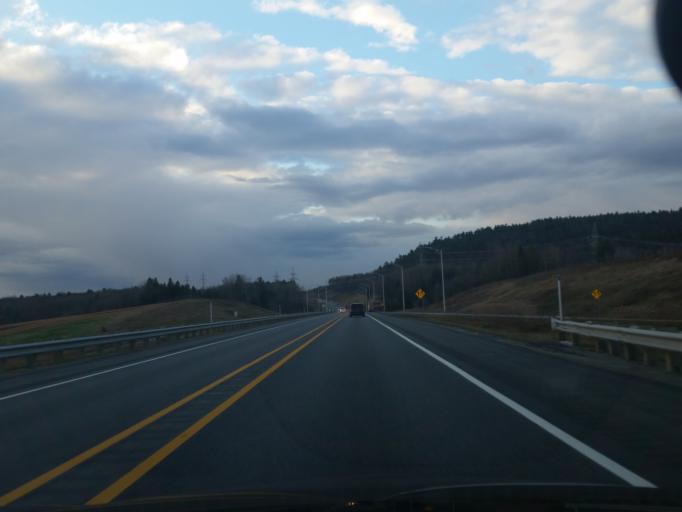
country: CA
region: Quebec
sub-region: Outaouais
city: Papineauville
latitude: 45.6591
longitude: -74.8703
